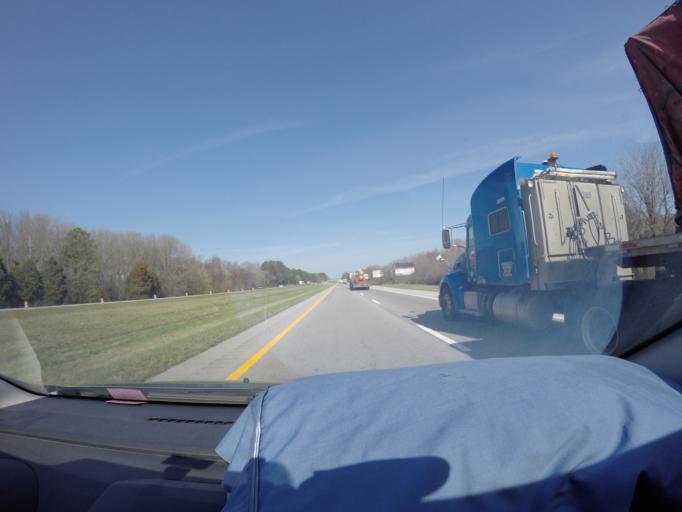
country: US
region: Tennessee
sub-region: Franklin County
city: Sewanee
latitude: 35.3574
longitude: -85.9555
